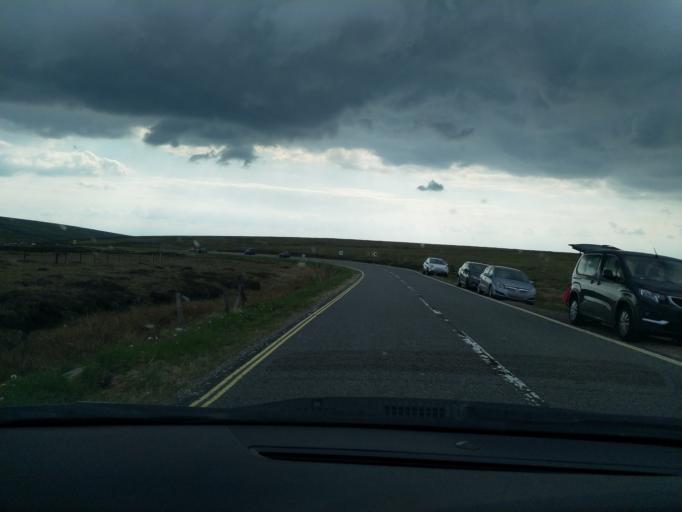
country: GB
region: England
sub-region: Derbyshire
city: High Peak
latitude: 53.4329
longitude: -1.8717
